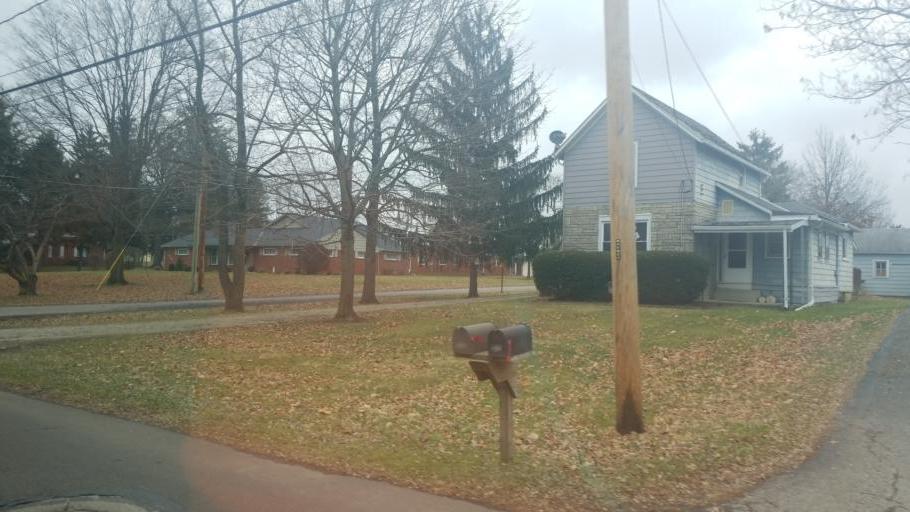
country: US
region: Ohio
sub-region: Crawford County
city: Galion
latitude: 40.7457
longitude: -82.7832
